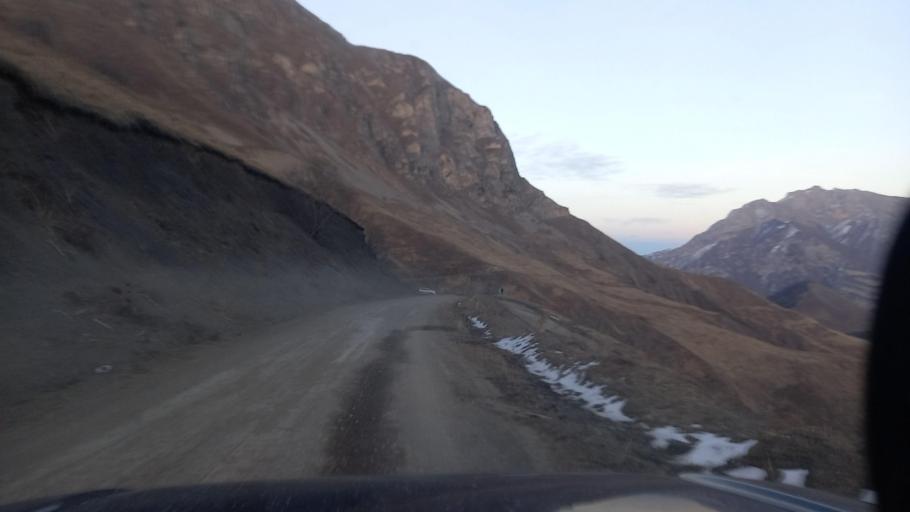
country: RU
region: Ingushetiya
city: Dzhayrakh
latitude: 42.8339
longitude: 44.5678
